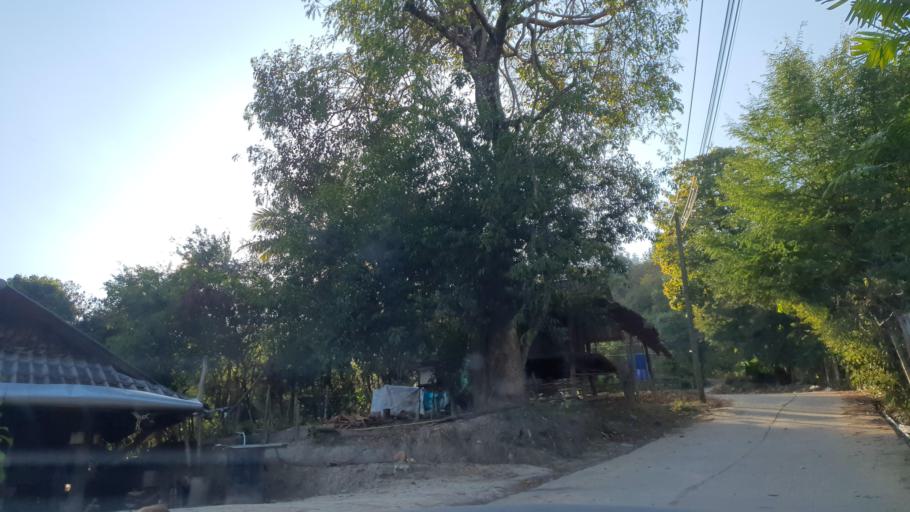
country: TH
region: Chiang Mai
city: Mae Wang
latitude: 18.6583
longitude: 98.6353
